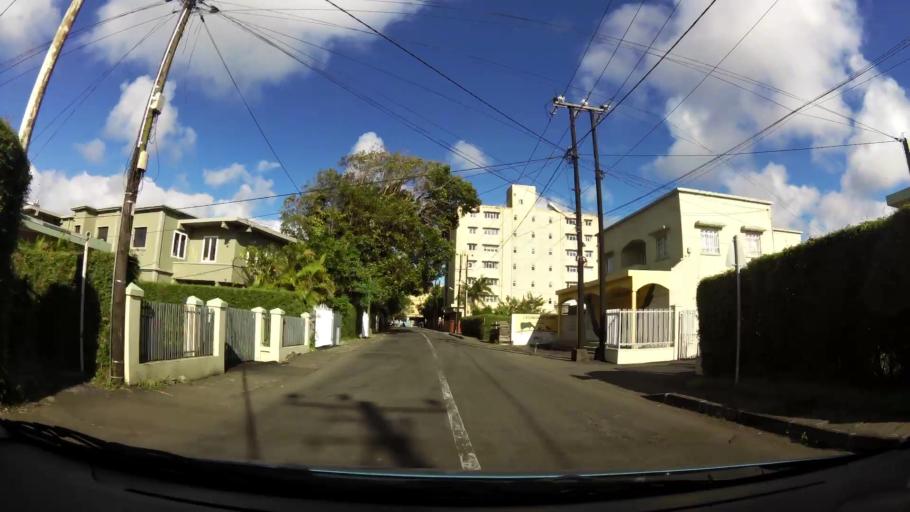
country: MU
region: Plaines Wilhems
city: Curepipe
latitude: -20.3184
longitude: 57.5301
